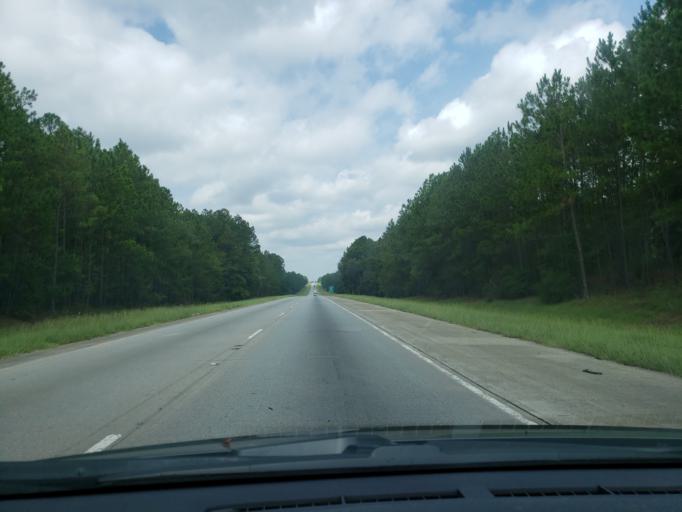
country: US
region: Georgia
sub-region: Emanuel County
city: Swainsboro
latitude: 32.4123
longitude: -82.3660
